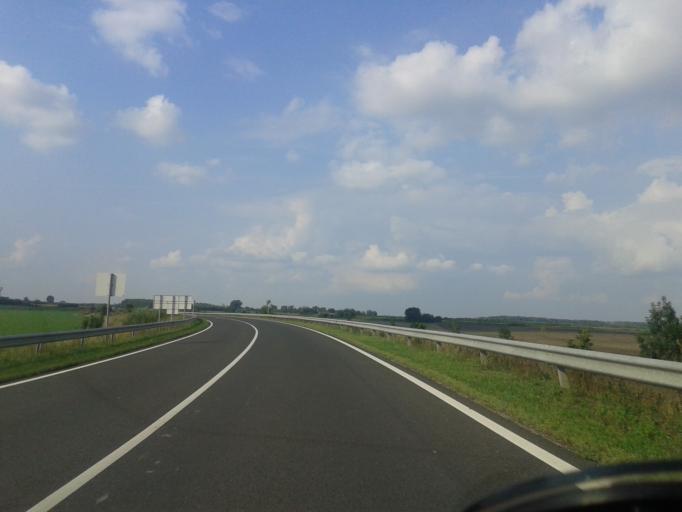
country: HU
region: Bacs-Kiskun
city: Dunavecse
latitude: 46.9033
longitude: 18.9902
